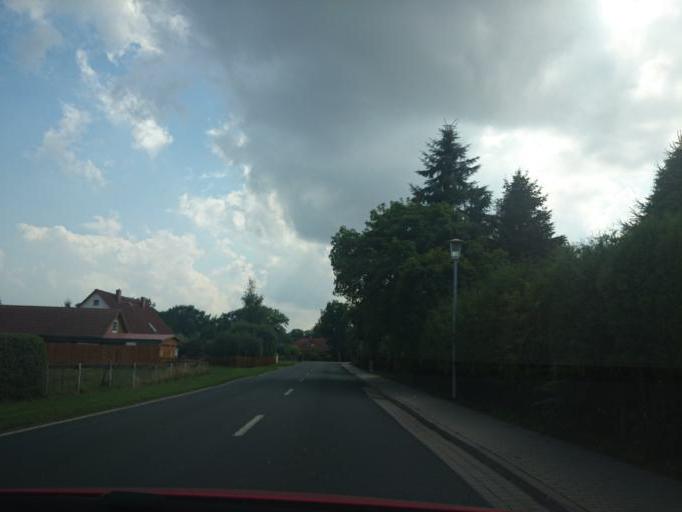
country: DE
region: Mecklenburg-Vorpommern
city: Velgast
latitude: 54.3049
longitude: 12.7924
